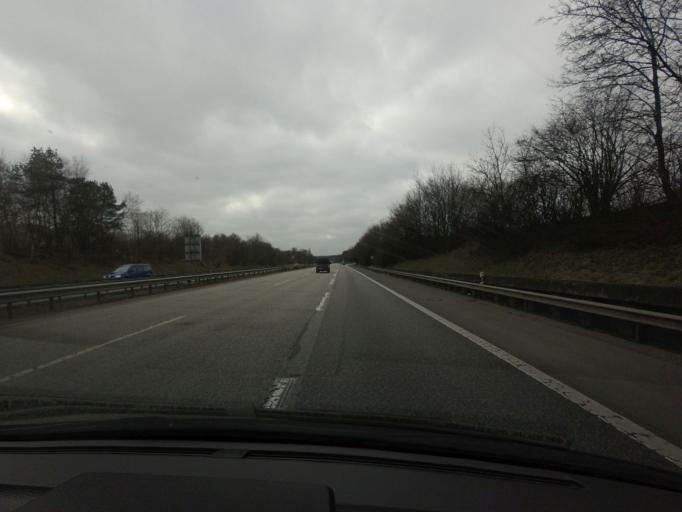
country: DE
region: Lower Saxony
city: Buchholz in der Nordheide
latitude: 53.3774
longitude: 9.8625
